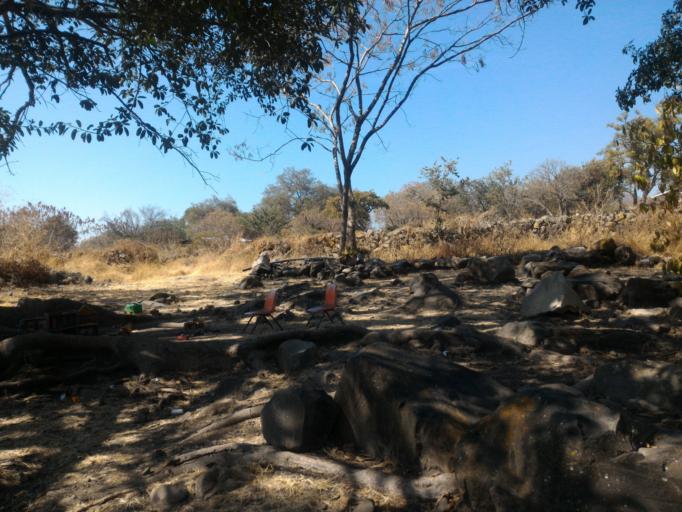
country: MX
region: Jalisco
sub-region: Poncitlan
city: Cuitzeo (La Estancia)
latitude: 20.3241
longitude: -102.7910
